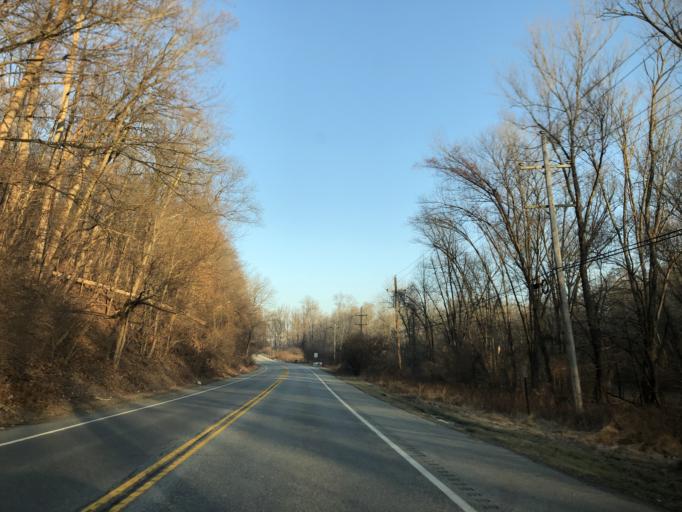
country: US
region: Pennsylvania
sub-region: Chester County
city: Downingtown
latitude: 39.9833
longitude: -75.6889
